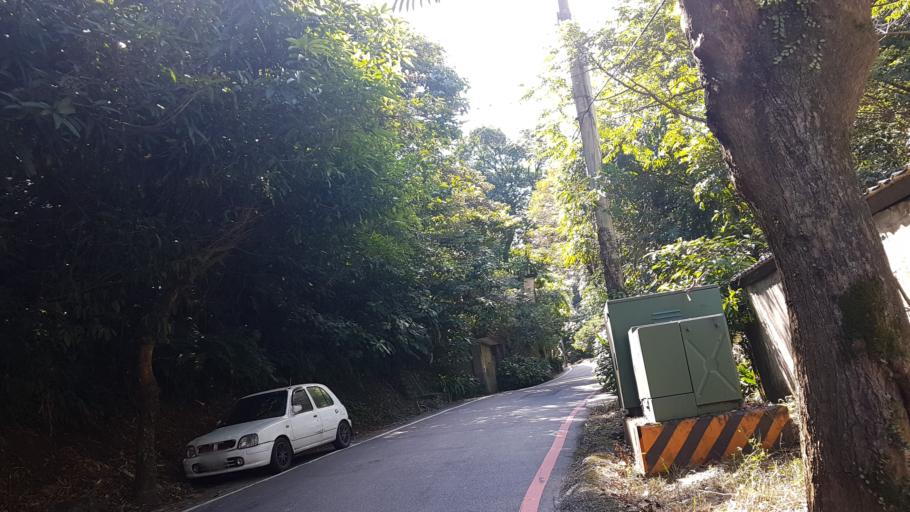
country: TW
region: Taipei
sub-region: Taipei
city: Banqiao
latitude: 24.9516
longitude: 121.5315
